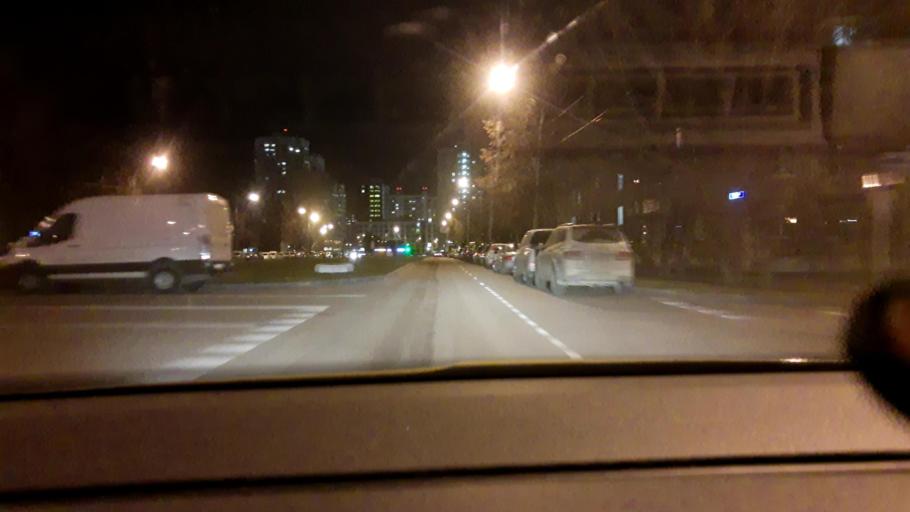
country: RU
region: Moscow
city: Vostochnyy
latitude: 55.8191
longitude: 37.8674
